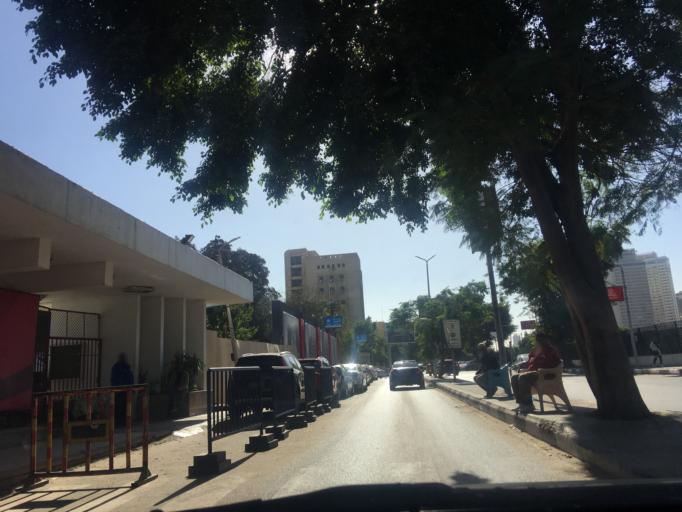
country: EG
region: Muhafazat al Qahirah
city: Cairo
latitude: 30.0449
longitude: 31.2206
